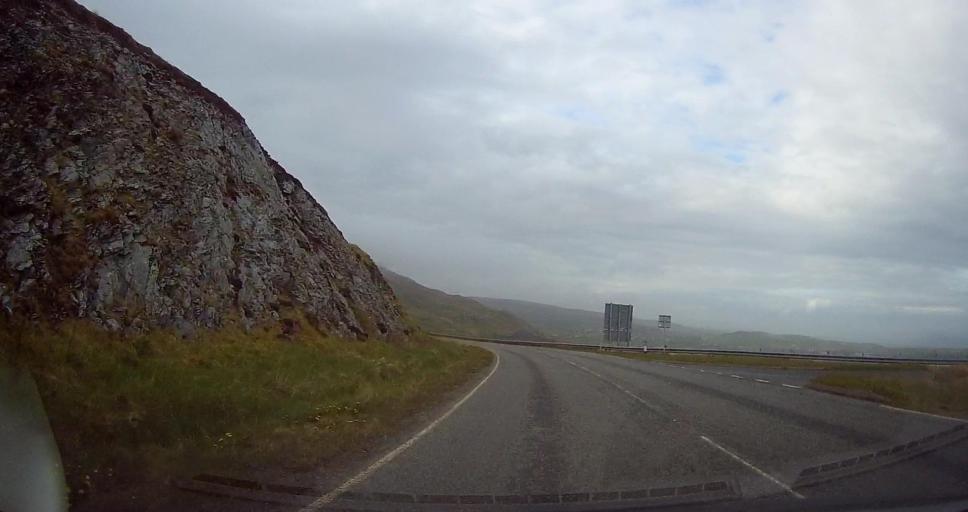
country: GB
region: Scotland
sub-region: Shetland Islands
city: Sandwick
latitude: 60.0185
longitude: -1.2312
